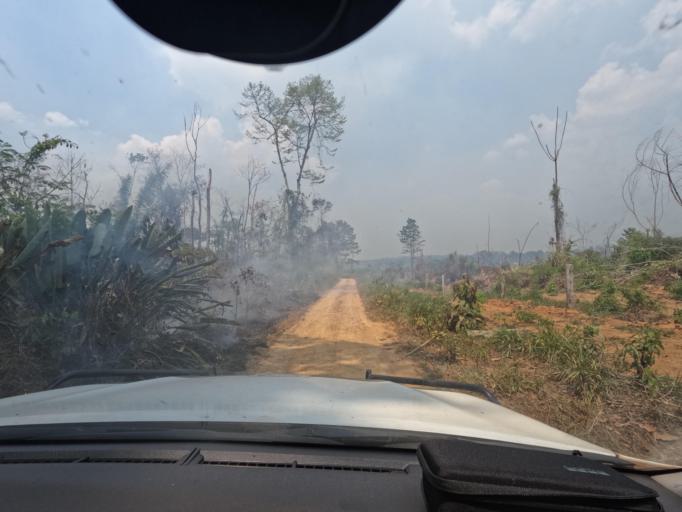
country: BR
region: Rondonia
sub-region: Porto Velho
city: Porto Velho
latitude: -8.7731
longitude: -63.1179
